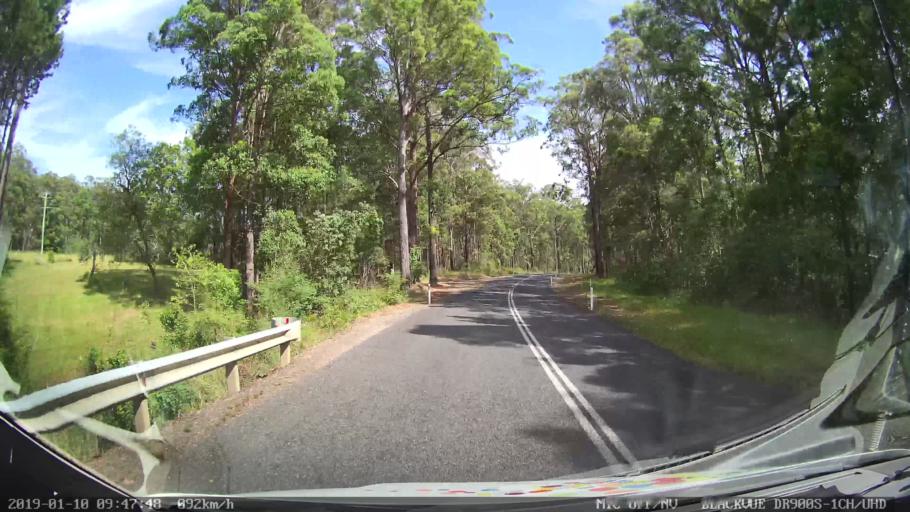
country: AU
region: New South Wales
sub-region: Coffs Harbour
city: Nana Glen
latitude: -30.0807
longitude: 152.9893
